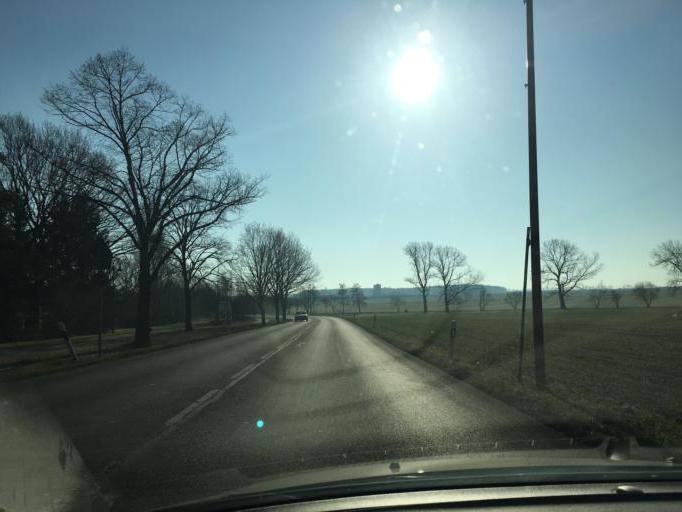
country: DE
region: Saxony
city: Grossposna
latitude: 51.2740
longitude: 12.4755
